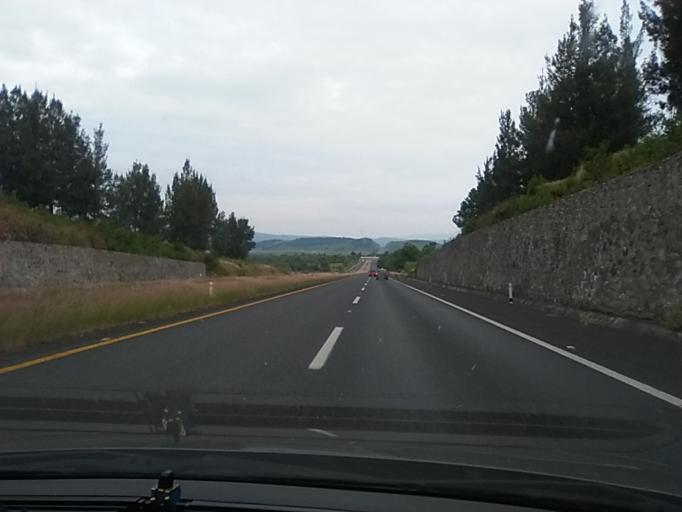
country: MX
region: Michoacan
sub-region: Puruandiro
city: San Lorenzo
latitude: 19.9559
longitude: -101.6600
